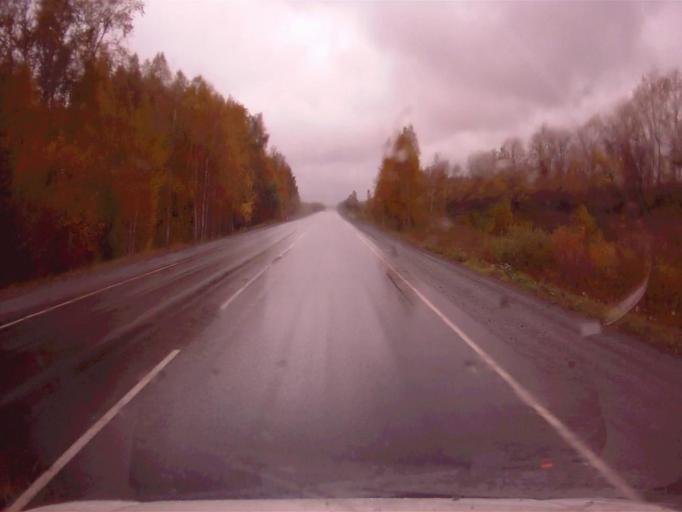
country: RU
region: Chelyabinsk
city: Argayash
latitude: 55.4358
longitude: 60.9767
